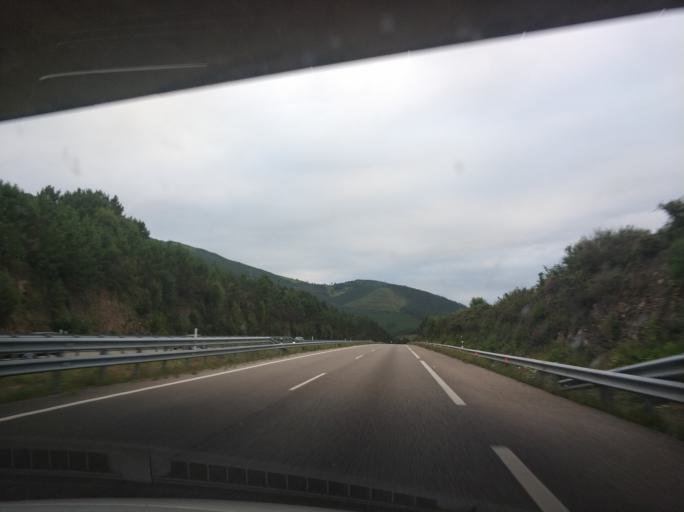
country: ES
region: Asturias
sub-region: Province of Asturias
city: Tineo
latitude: 43.5375
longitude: -6.4803
